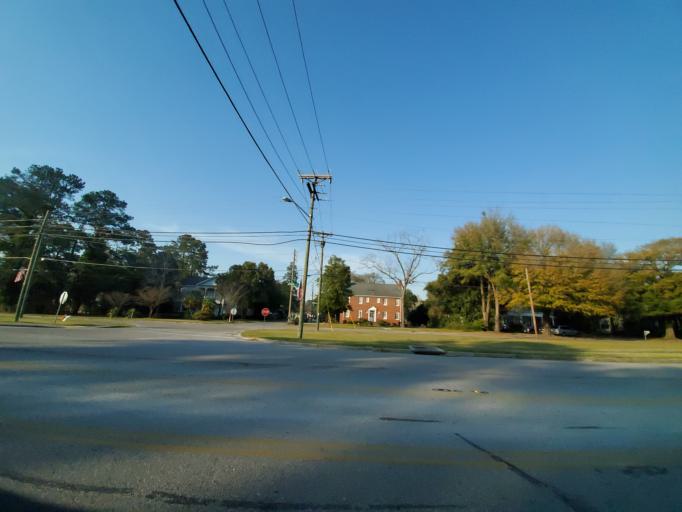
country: US
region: South Carolina
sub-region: Bamberg County
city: Bamberg
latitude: 33.2961
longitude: -81.0317
